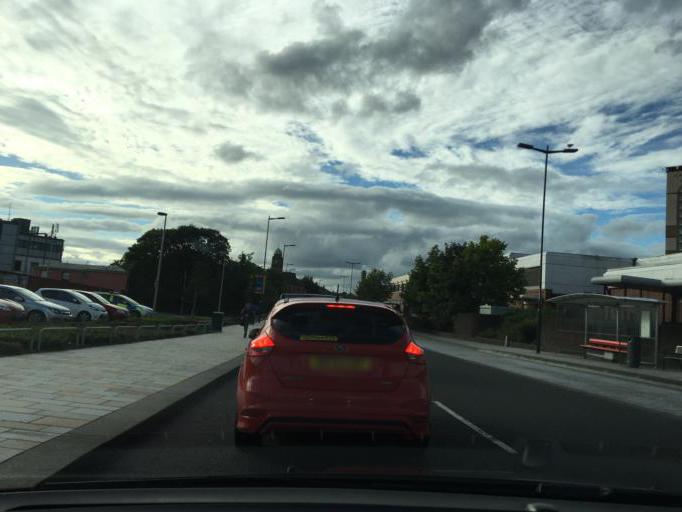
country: GB
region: Scotland
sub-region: North Lanarkshire
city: Motherwell
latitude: 55.7882
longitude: -3.9905
